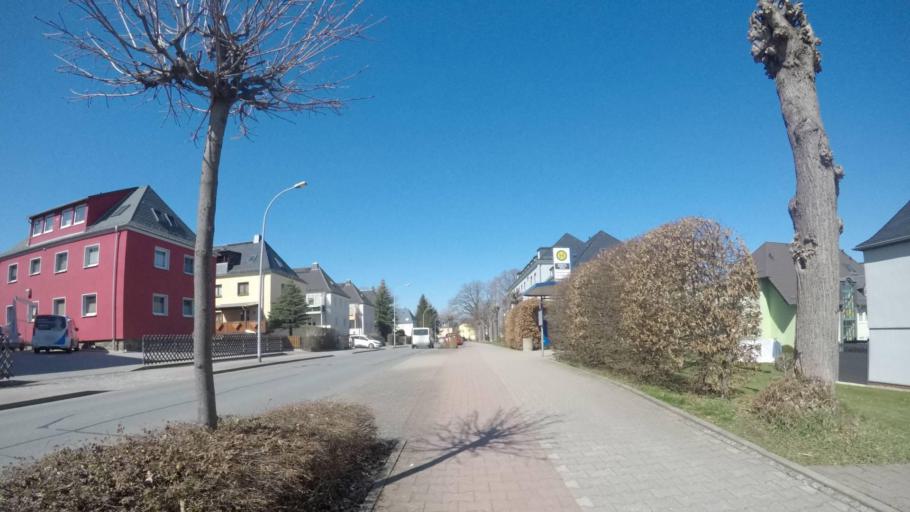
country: DE
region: Saxony
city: Limbach-Oberfrohna
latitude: 50.8646
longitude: 12.7541
